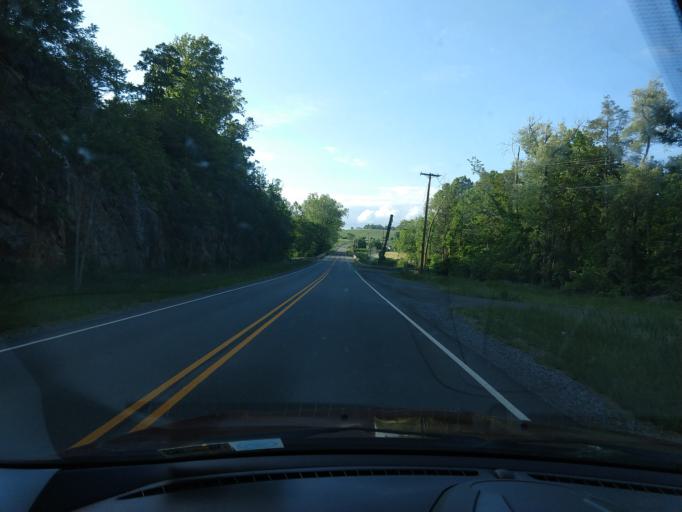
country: US
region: Virginia
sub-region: Wythe County
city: Wytheville
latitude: 36.8511
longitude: -80.9762
